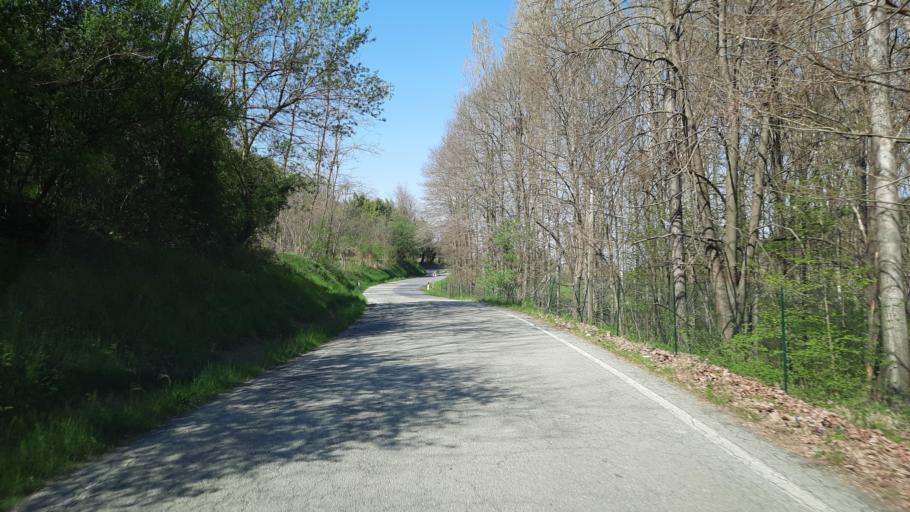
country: IT
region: Piedmont
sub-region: Provincia di Alessandria
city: Moncestino
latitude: 45.1471
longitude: 8.1281
